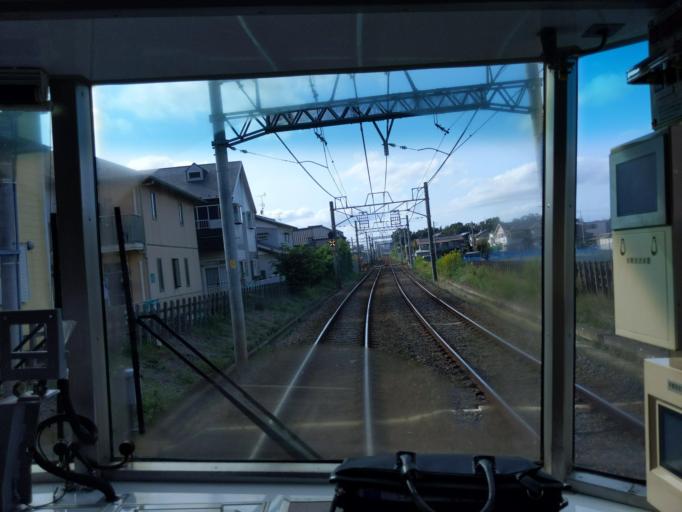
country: JP
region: Chiba
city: Kashiwa
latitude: 35.7765
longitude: 139.9847
